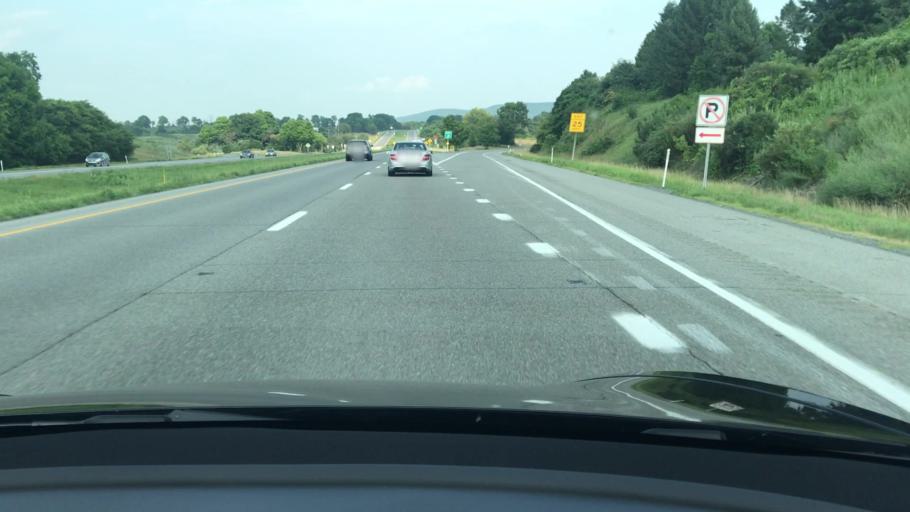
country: US
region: Pennsylvania
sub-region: Centre County
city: Boalsburg
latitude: 40.7896
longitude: -77.8059
